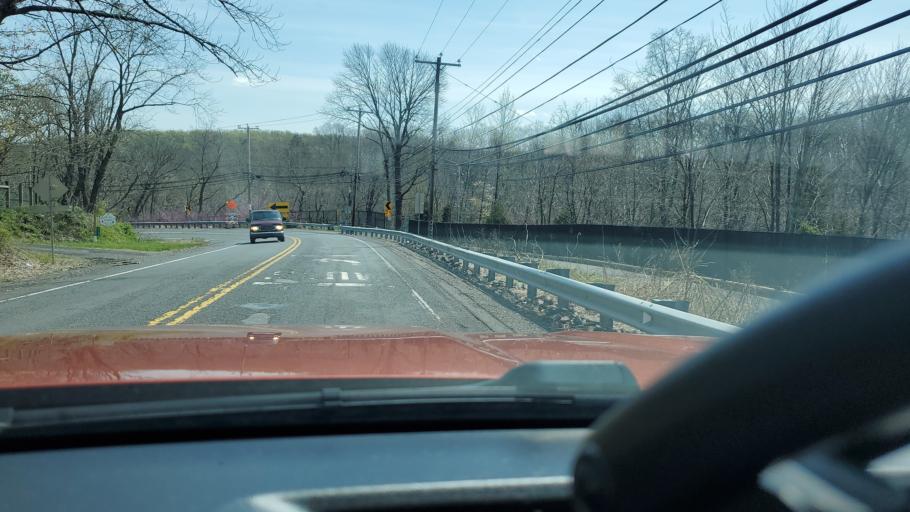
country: US
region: Pennsylvania
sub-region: Montgomery County
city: Red Hill
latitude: 40.3417
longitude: -75.4775
